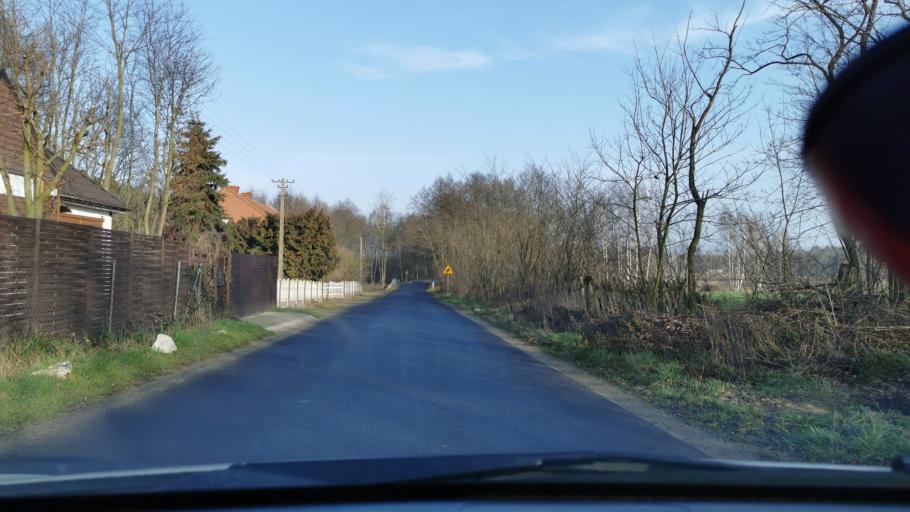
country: PL
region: Greater Poland Voivodeship
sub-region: Powiat kaliski
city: Opatowek
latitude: 51.6591
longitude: 18.2500
